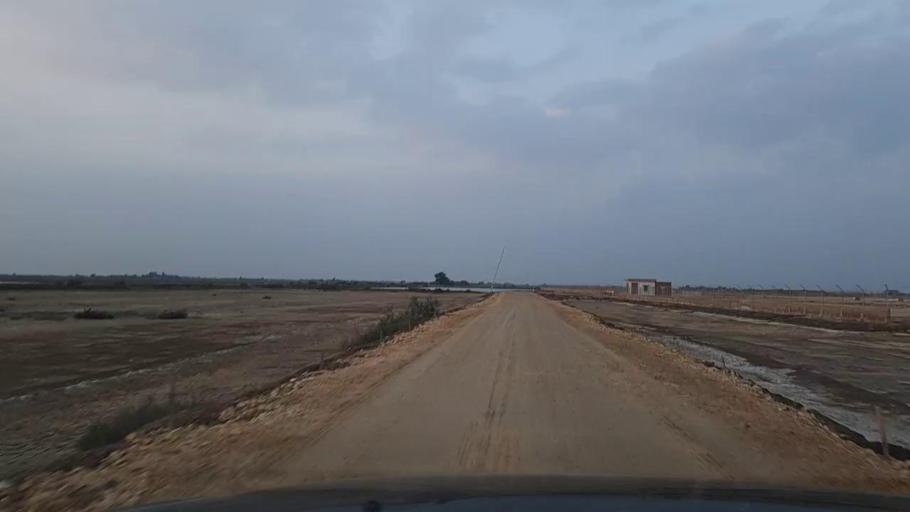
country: PK
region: Sindh
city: Jati
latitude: 24.4928
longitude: 68.3918
